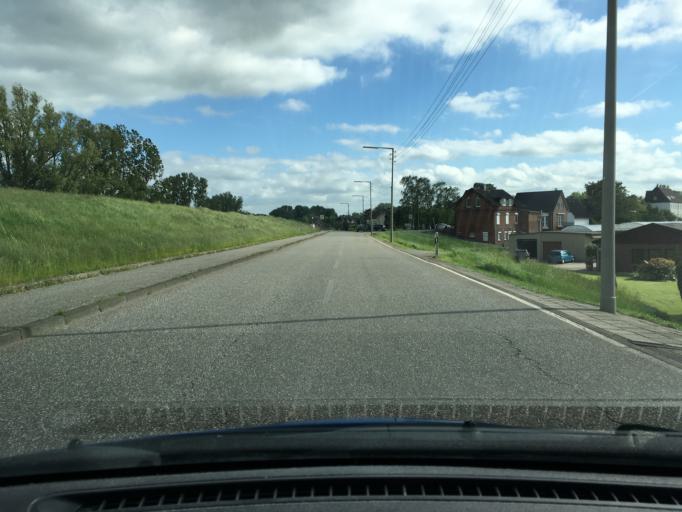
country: DE
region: Hamburg
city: Rothenburgsort
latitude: 53.4687
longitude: 10.0606
